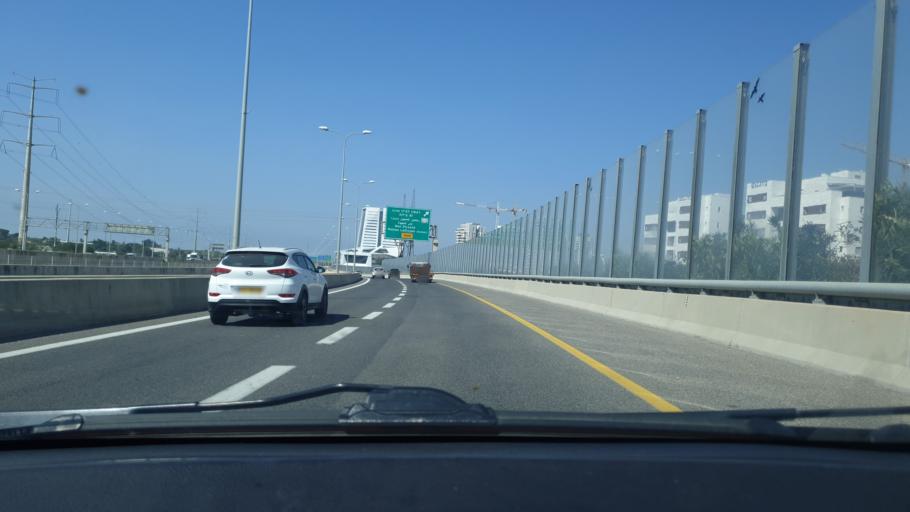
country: IL
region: Central District
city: Ness Ziona
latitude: 31.9463
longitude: 34.8120
